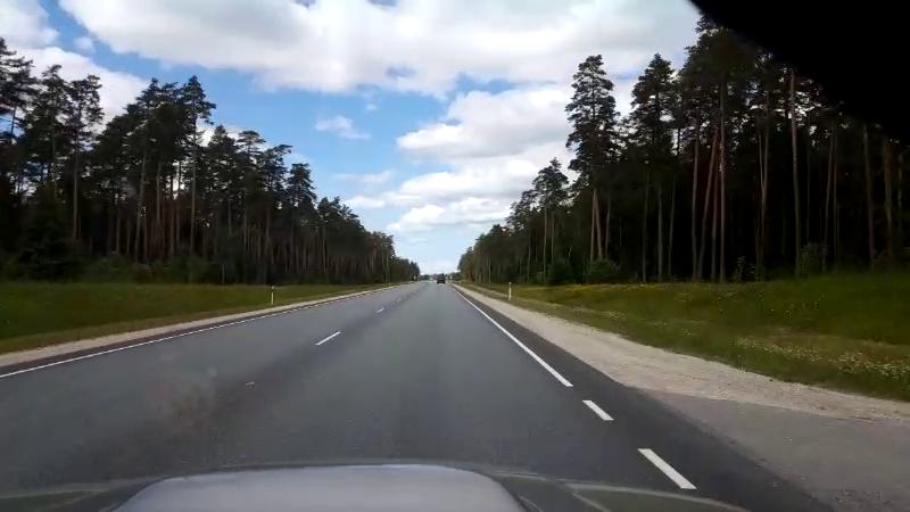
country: EE
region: Raplamaa
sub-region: Maerjamaa vald
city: Marjamaa
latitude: 59.0176
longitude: 24.4525
